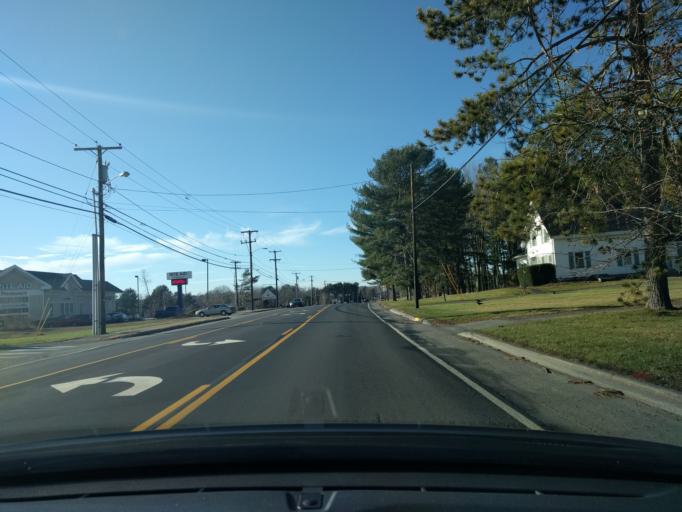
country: US
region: Maine
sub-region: Penobscot County
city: Hampden
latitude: 44.7449
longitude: -68.8430
